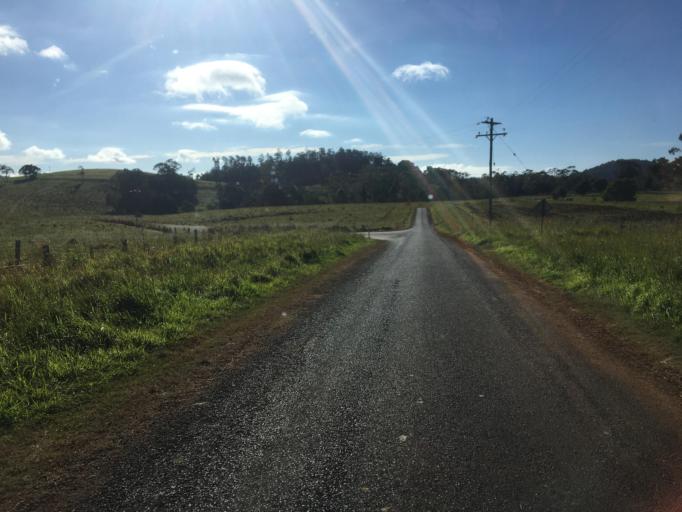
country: AU
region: Queensland
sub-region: Tablelands
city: Ravenshoe
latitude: -17.6074
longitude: 145.5440
